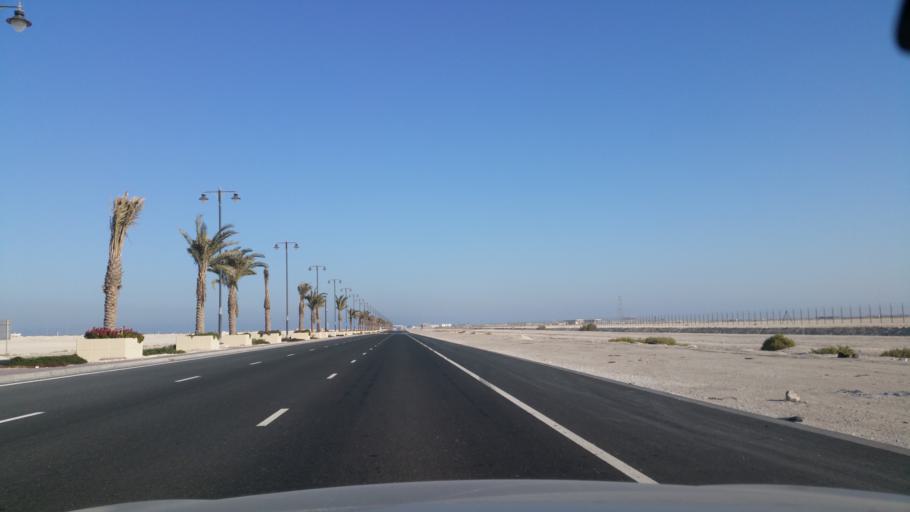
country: QA
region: Al Wakrah
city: Umm Sa'id
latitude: 25.0597
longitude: 51.5891
